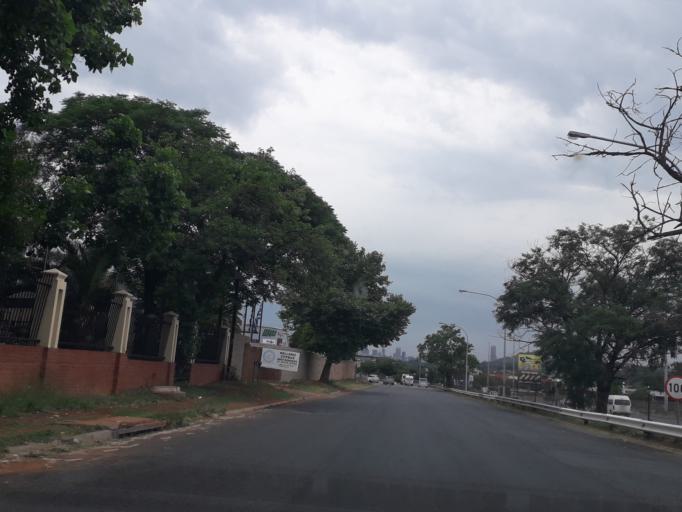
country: ZA
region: Gauteng
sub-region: City of Johannesburg Metropolitan Municipality
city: Johannesburg
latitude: -26.1766
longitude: 28.1198
